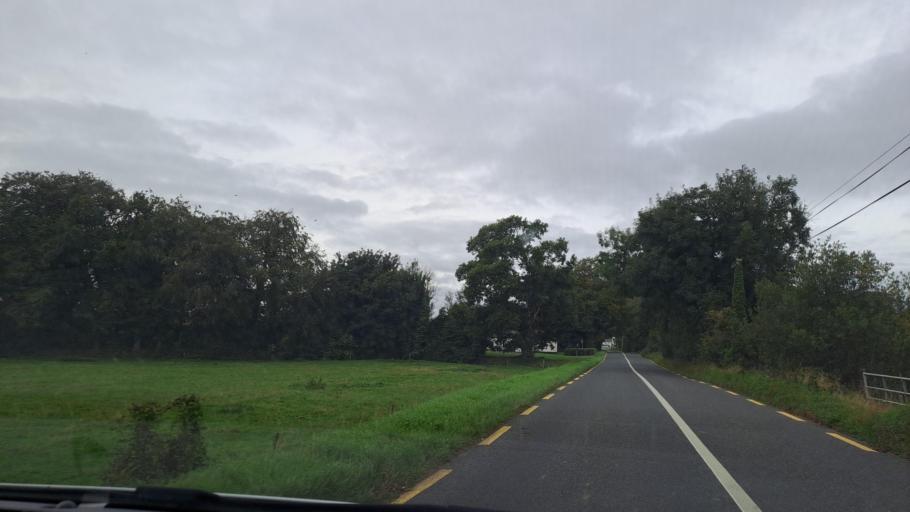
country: IE
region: Leinster
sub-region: Lu
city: Ardee
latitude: 53.8478
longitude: -6.6282
